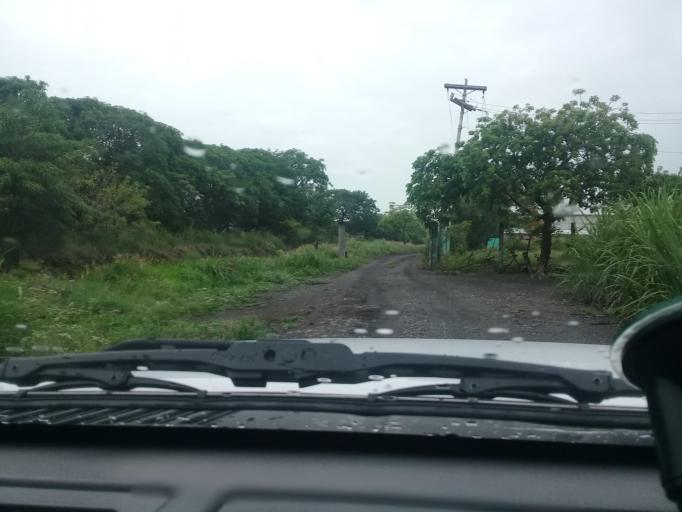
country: MX
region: Veracruz
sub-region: Puente Nacional
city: Cabezas
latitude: 19.3635
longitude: -96.4037
